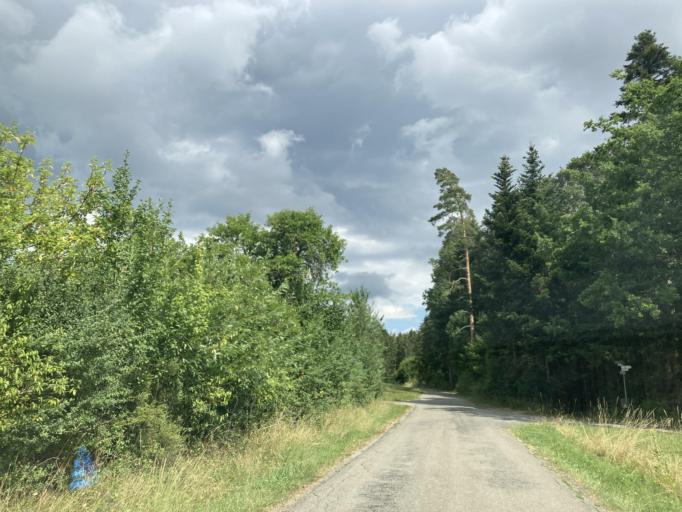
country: DE
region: Baden-Wuerttemberg
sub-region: Karlsruhe Region
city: Ebhausen
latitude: 48.6102
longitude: 8.6606
